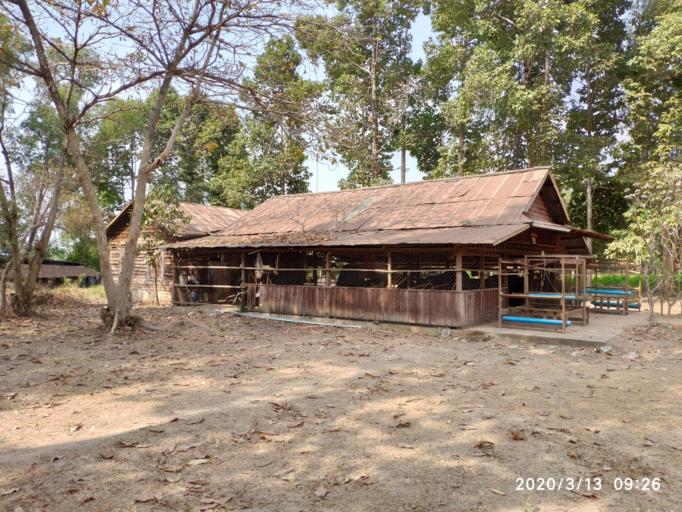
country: KH
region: Siem Reap
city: Siem Reap
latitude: 13.4371
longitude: 103.7446
